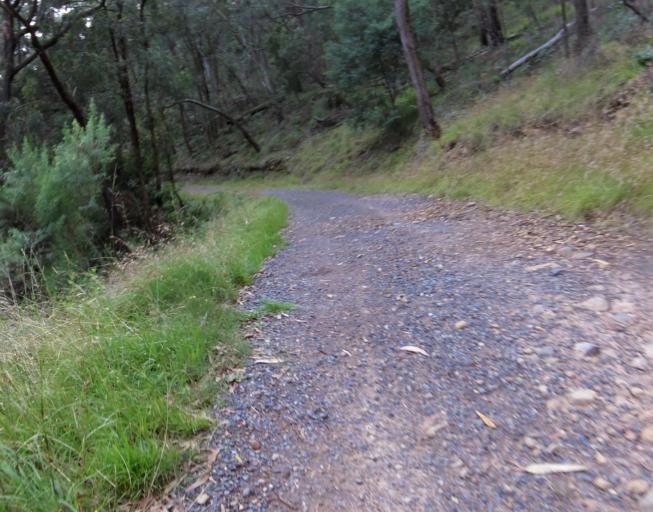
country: AU
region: Victoria
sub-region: Yarra Ranges
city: Montrose
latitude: -37.8311
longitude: 145.3436
